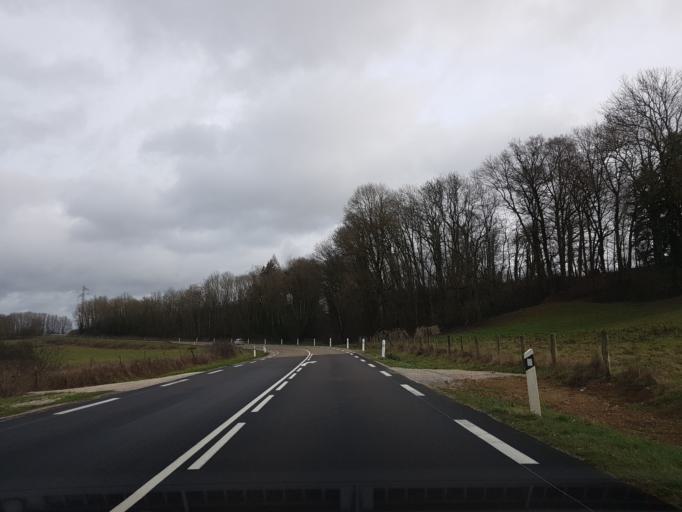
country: FR
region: Champagne-Ardenne
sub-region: Departement de la Haute-Marne
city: Langres
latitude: 47.8567
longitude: 5.3811
